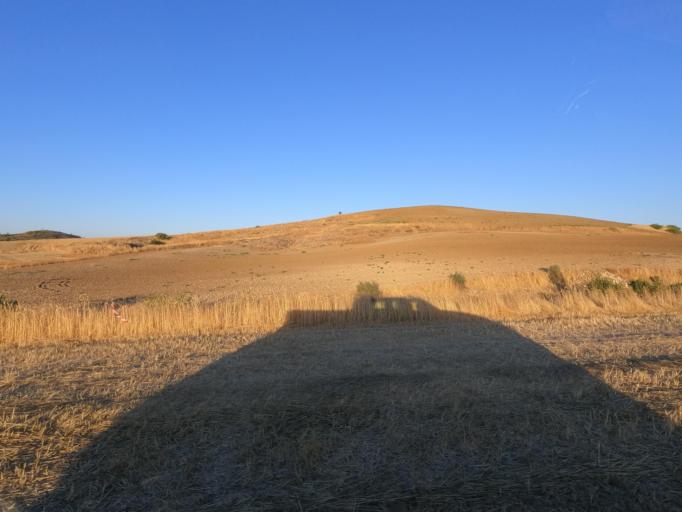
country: CY
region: Larnaka
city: Troulloi
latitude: 35.0276
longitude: 33.6366
